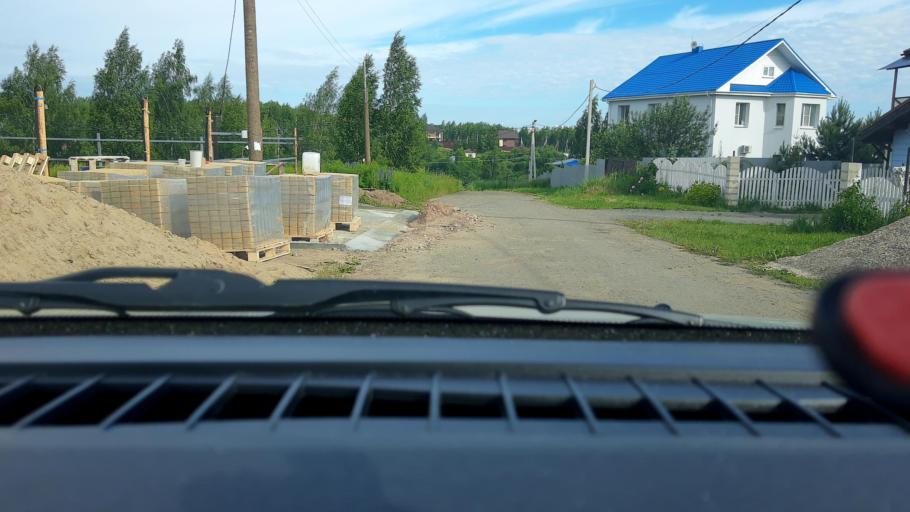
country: RU
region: Nizjnij Novgorod
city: Afonino
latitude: 56.2490
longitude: 44.0695
